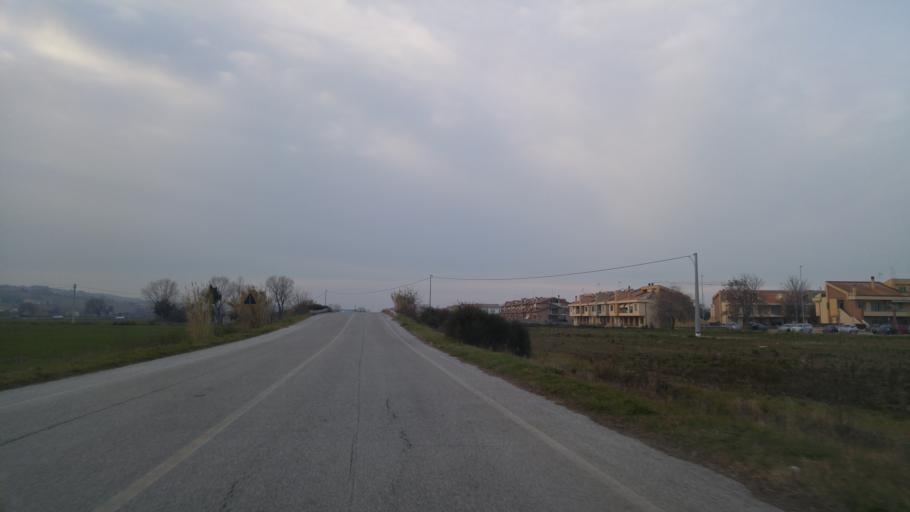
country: IT
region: The Marches
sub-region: Provincia di Pesaro e Urbino
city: Marotta
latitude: 43.7608
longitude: 13.1423
